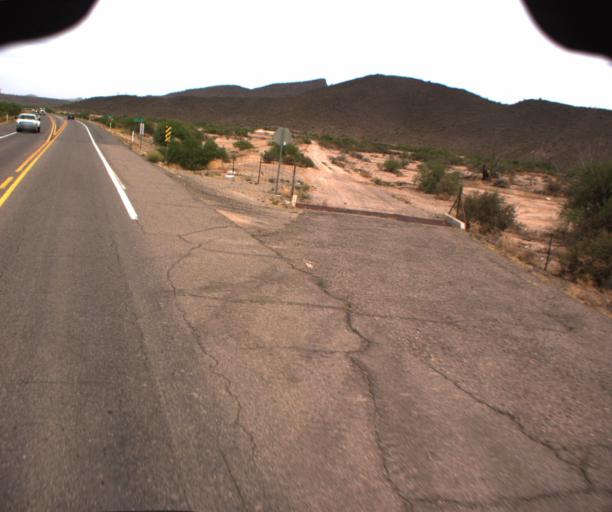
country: US
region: Arizona
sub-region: Pinal County
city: Sacaton
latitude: 33.1003
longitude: -111.7118
